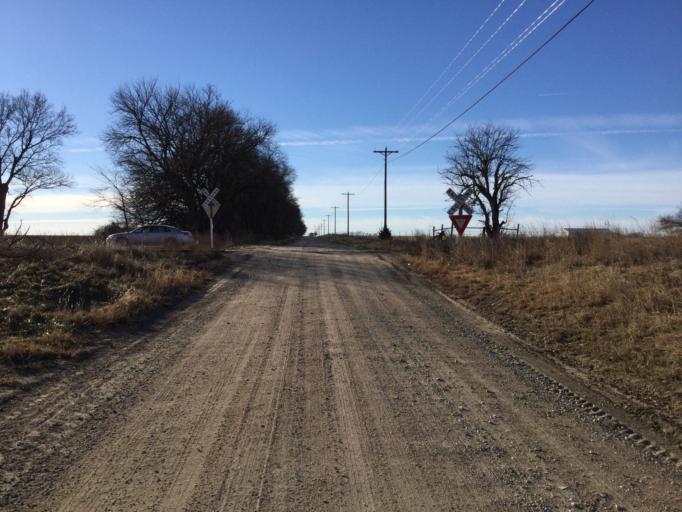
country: US
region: Kansas
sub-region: Butler County
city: Andover
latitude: 37.7889
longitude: -97.1531
